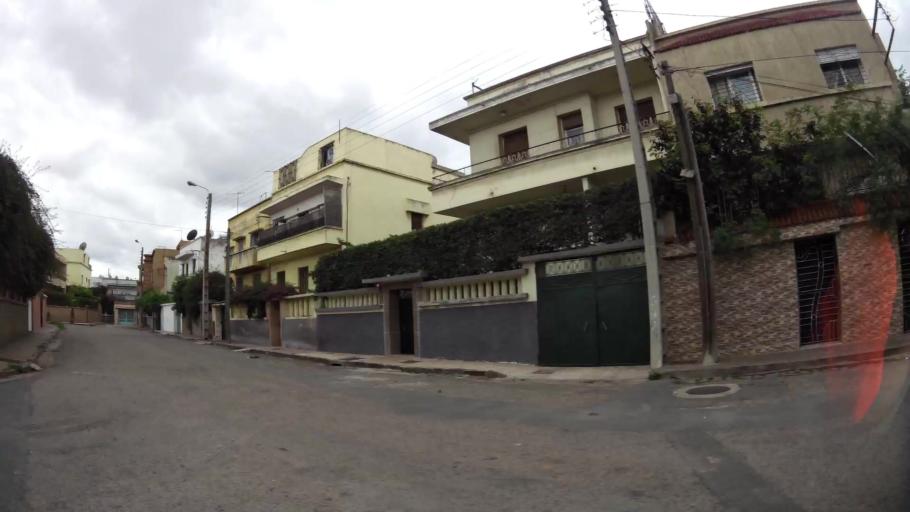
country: MA
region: Grand Casablanca
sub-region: Casablanca
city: Casablanca
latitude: 33.5673
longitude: -7.6166
